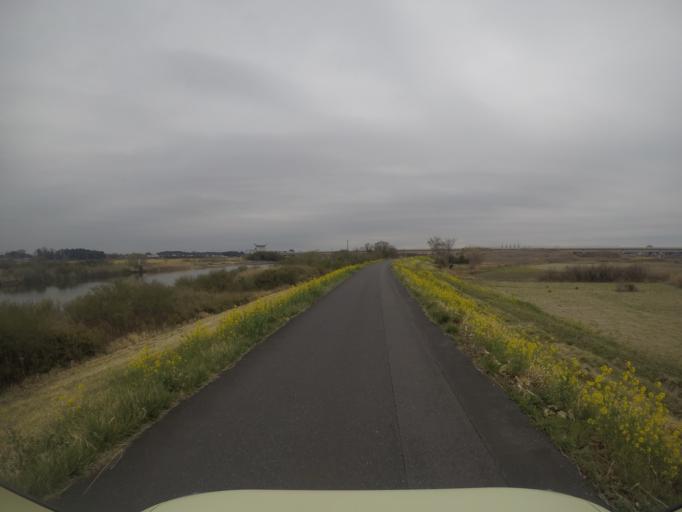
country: JP
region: Ibaraki
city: Ishige
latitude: 36.0830
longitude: 140.0013
